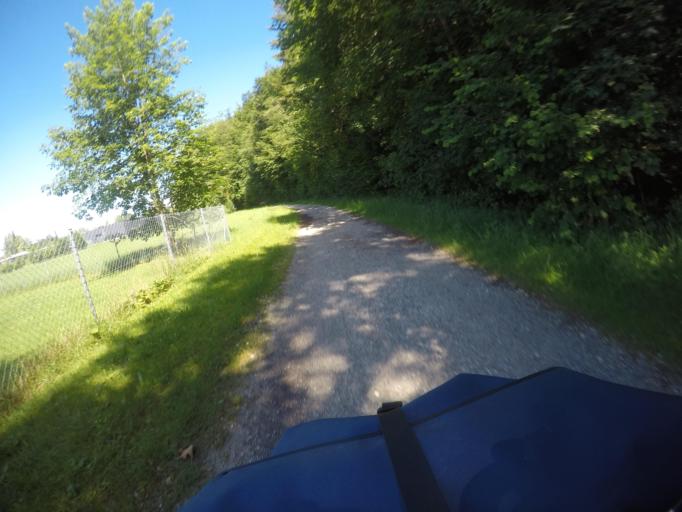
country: DE
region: Bavaria
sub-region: Swabia
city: Fuessen
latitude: 47.5668
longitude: 10.6828
